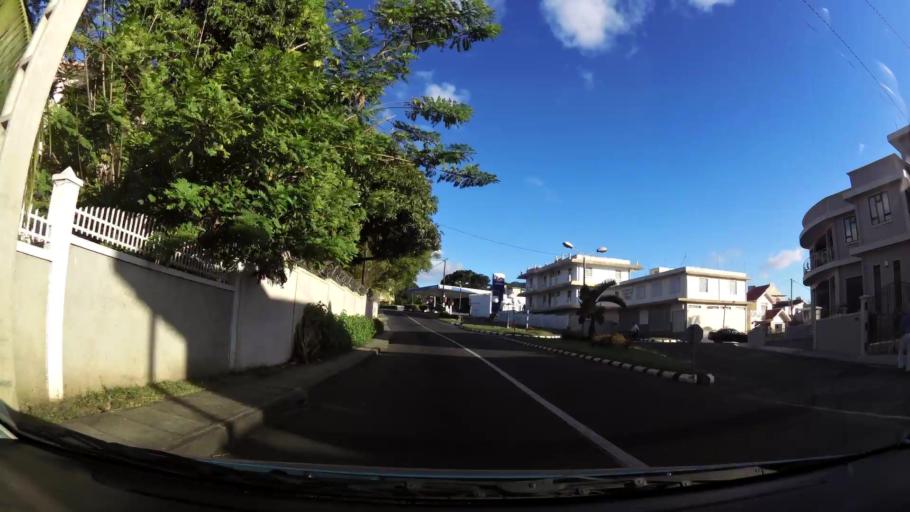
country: MU
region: Plaines Wilhems
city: Ebene
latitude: -20.2355
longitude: 57.4628
